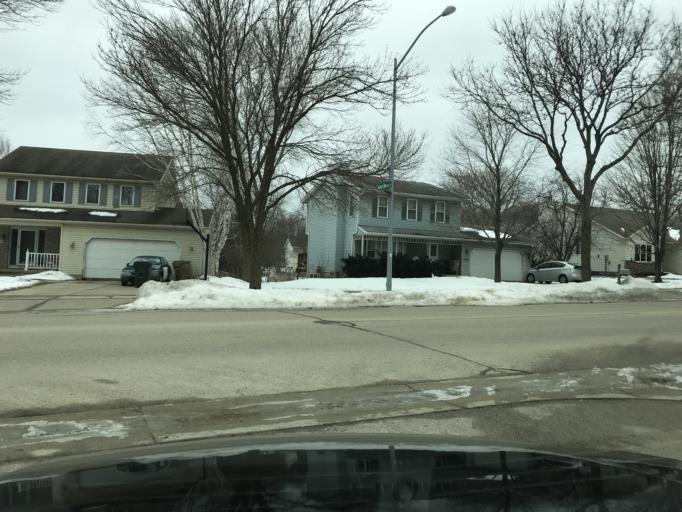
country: US
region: Wisconsin
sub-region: Dane County
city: Monona
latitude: 43.0696
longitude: -89.2813
